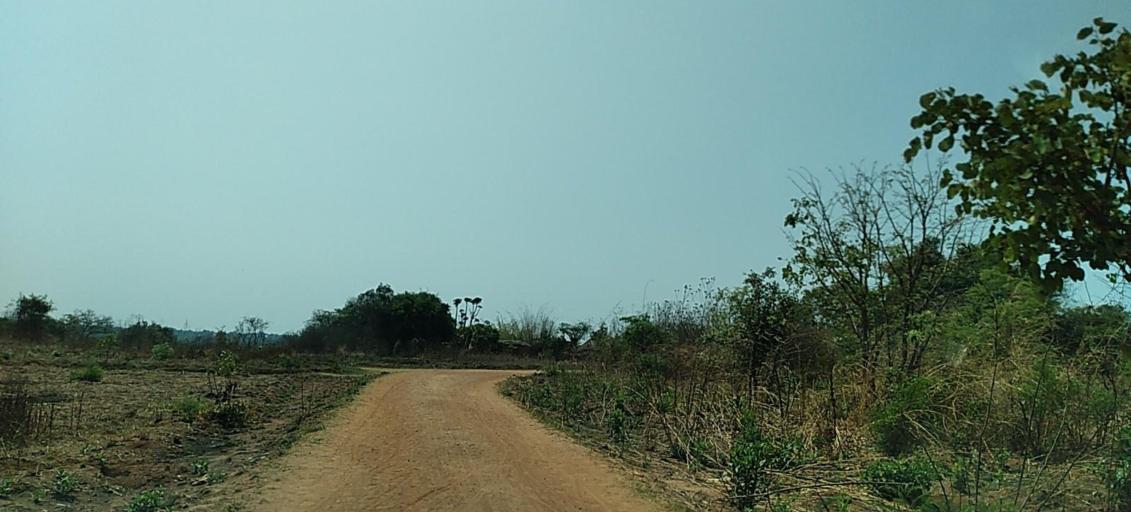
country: ZM
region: Copperbelt
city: Luanshya
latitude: -13.3417
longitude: 28.3914
